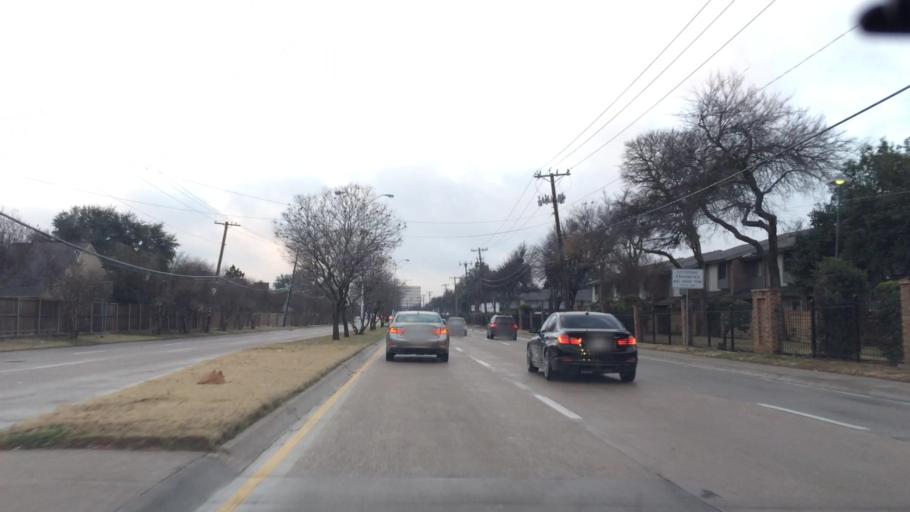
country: US
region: Texas
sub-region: Dallas County
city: Addison
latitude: 32.9592
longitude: -96.8046
